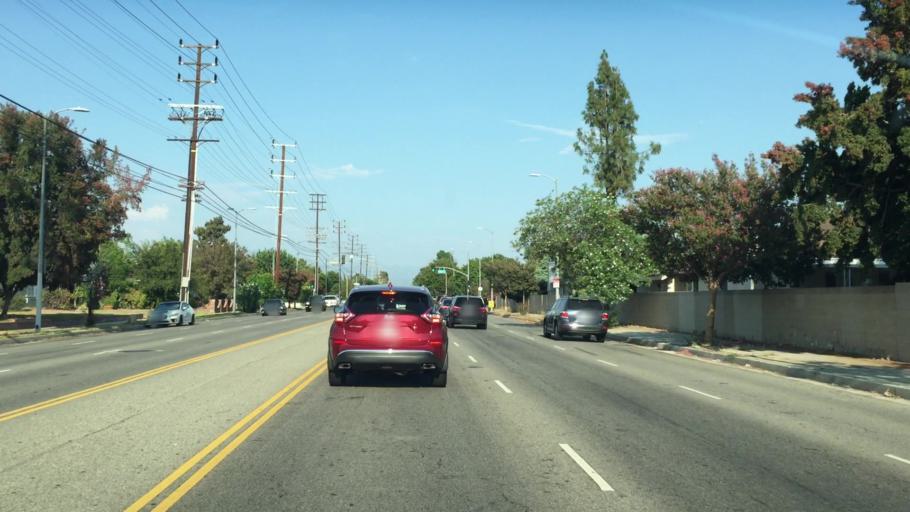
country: US
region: California
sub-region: Los Angeles County
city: Northridge
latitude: 34.2357
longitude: -118.4997
